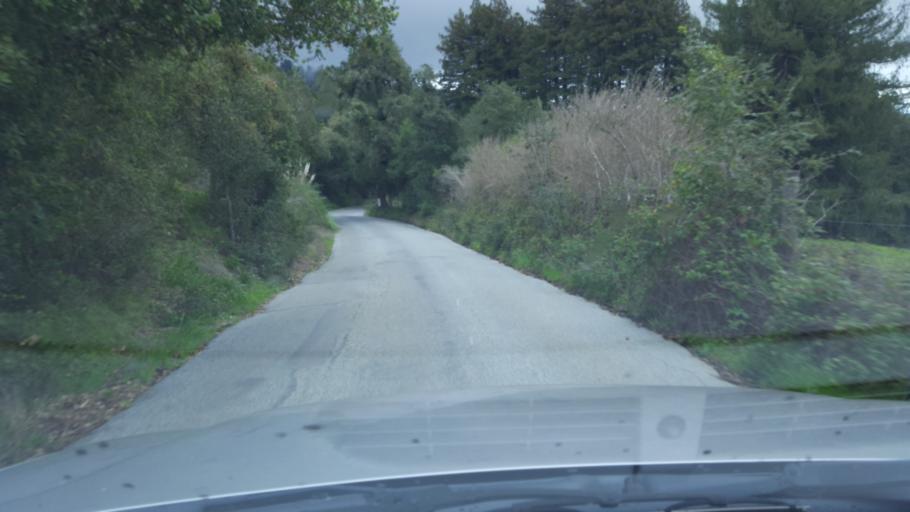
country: US
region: California
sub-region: Santa Cruz County
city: Interlaken
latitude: 37.0007
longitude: -121.7314
